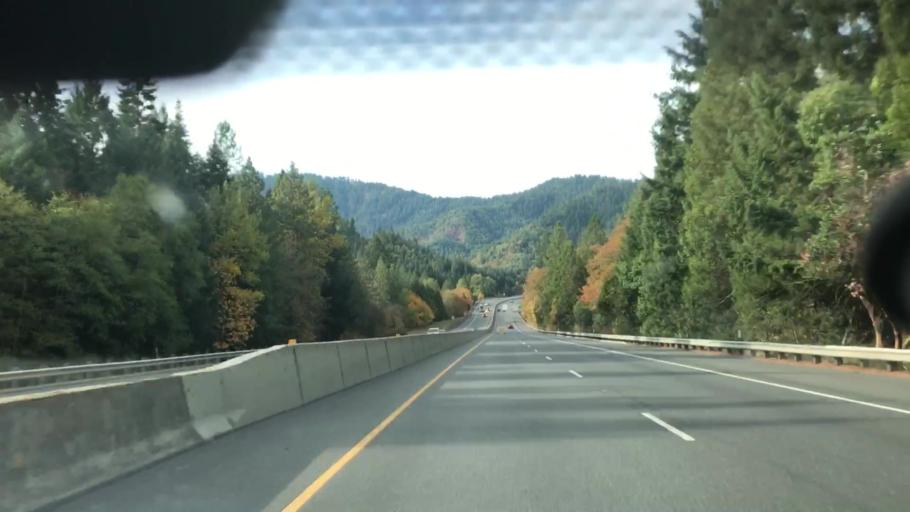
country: US
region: Oregon
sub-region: Josephine County
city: Merlin
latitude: 42.6834
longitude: -123.3869
